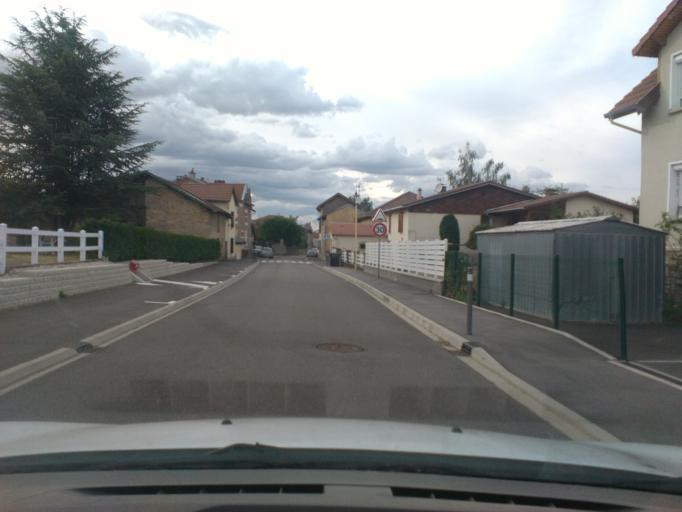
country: FR
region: Lorraine
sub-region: Departement des Vosges
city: Portieux
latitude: 48.3421
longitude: 6.3461
